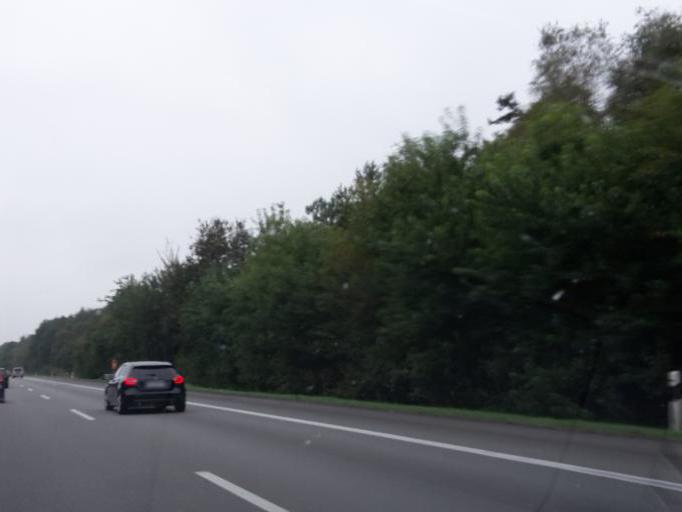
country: DE
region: Lower Saxony
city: Rieste
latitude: 52.4418
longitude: 8.0359
